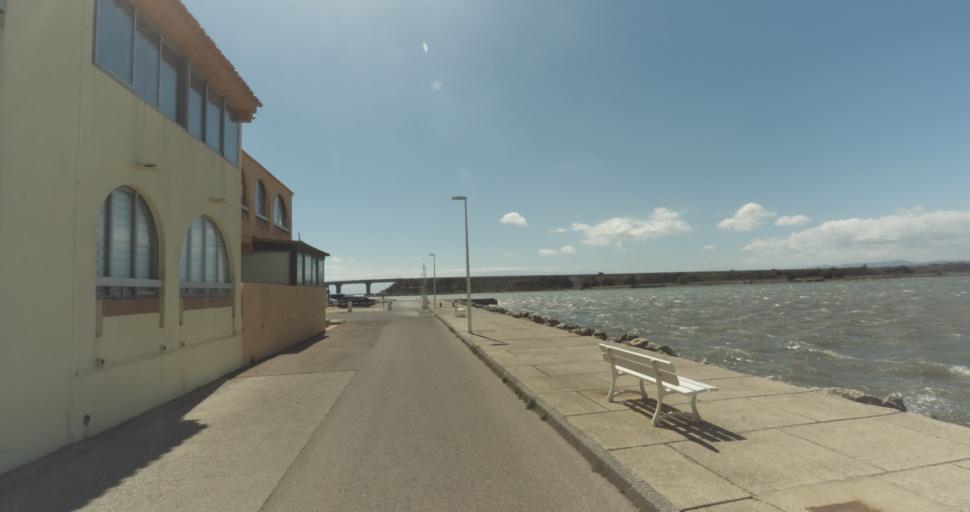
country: FR
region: Languedoc-Roussillon
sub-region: Departement de l'Aude
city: Leucate
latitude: 42.8604
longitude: 3.0353
